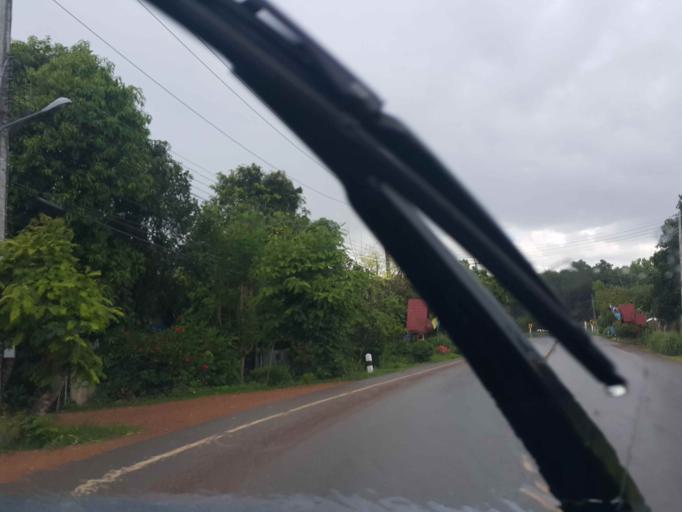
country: TH
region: Phayao
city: Dok Kham Tai
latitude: 19.0485
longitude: 100.0552
